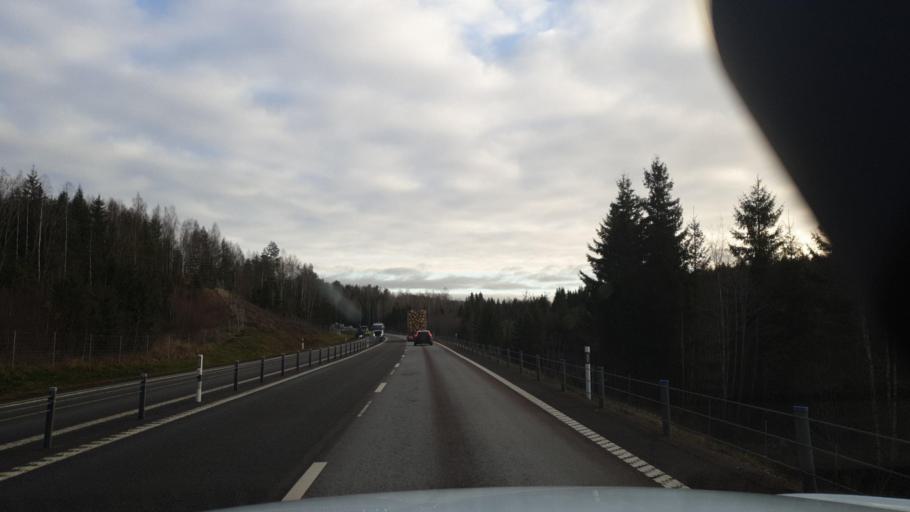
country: SE
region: Vaermland
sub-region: Arvika Kommun
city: Arvika
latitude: 59.6437
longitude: 12.7335
